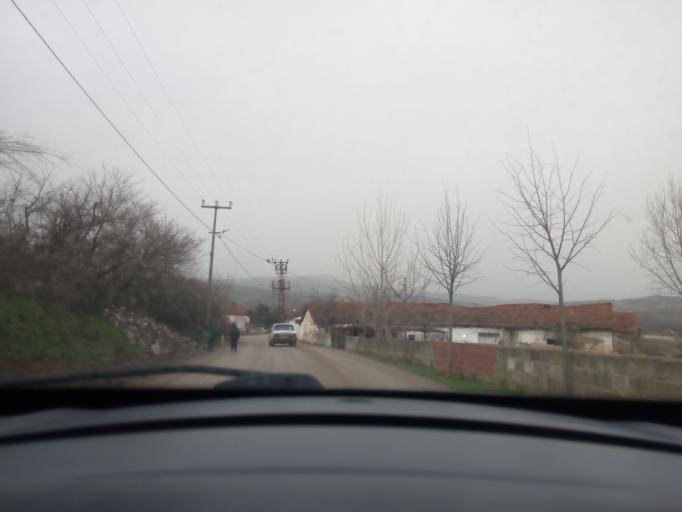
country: TR
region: Balikesir
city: Susurluk
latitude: 39.9203
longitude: 28.1480
